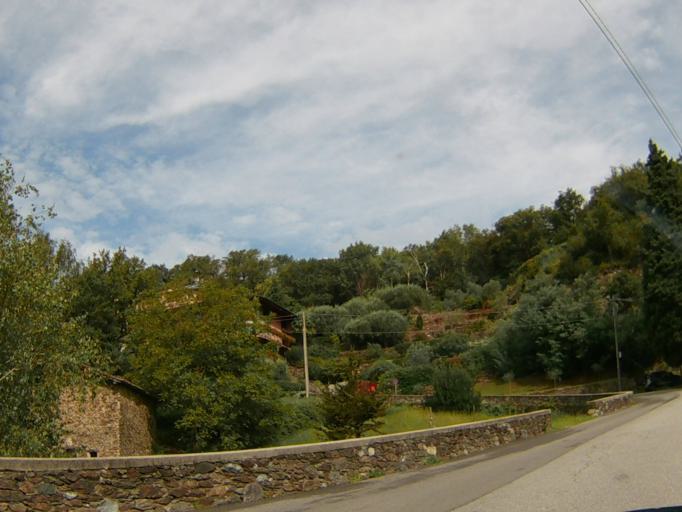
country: IT
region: Lombardy
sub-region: Provincia di Lecco
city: Dorio
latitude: 46.1154
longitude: 9.3189
